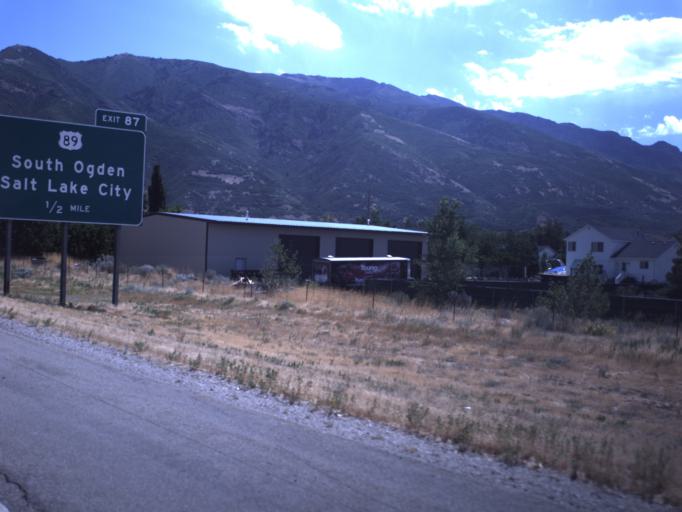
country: US
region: Utah
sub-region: Davis County
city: South Weber
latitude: 41.1363
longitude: -111.9284
